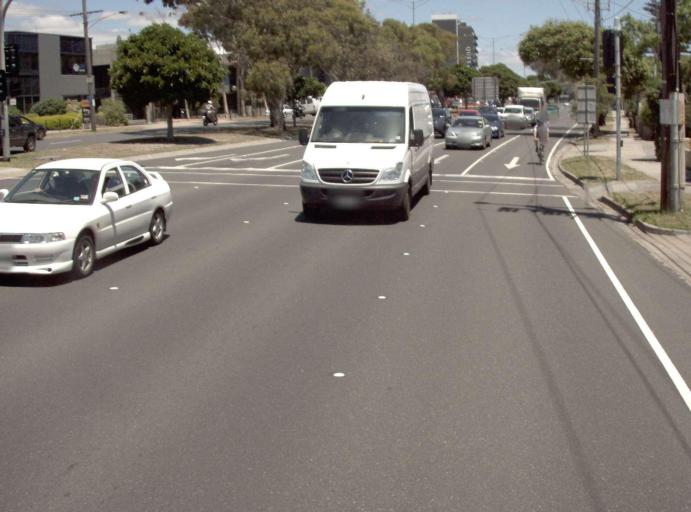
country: AU
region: Victoria
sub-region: Frankston
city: Frankston
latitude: -38.1385
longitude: 145.1232
